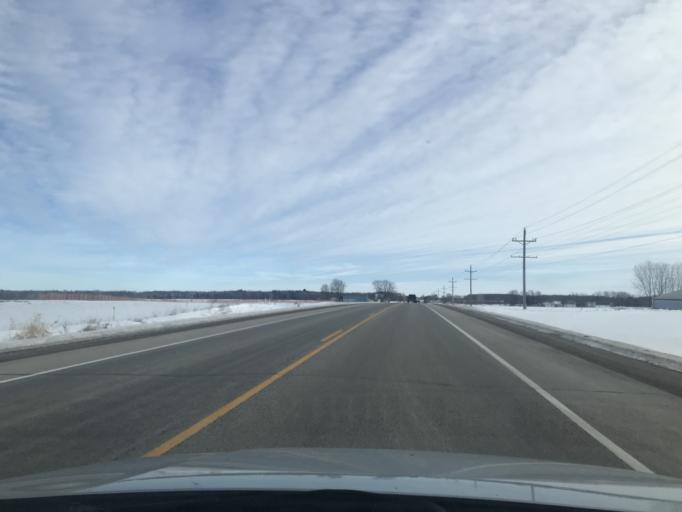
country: US
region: Wisconsin
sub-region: Oconto County
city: Gillett
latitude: 44.8958
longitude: -88.2252
